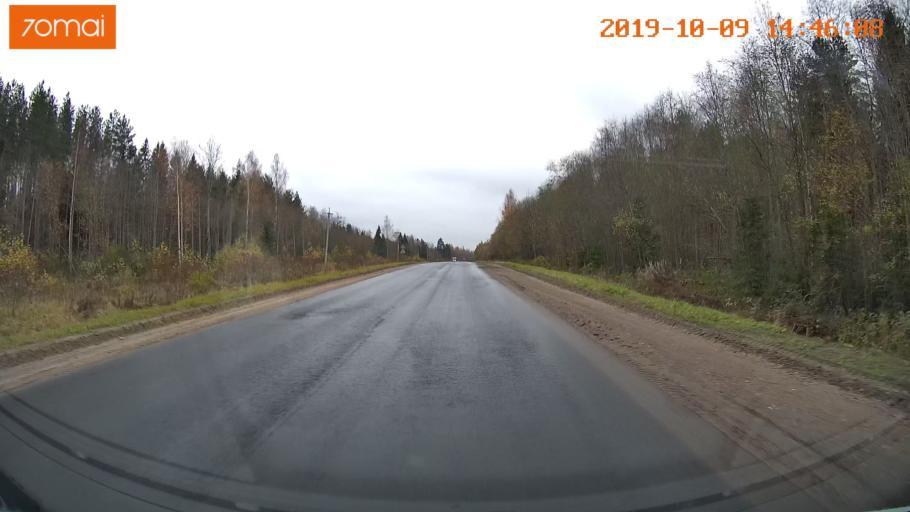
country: RU
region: Kostroma
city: Buy
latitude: 58.4352
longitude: 41.5772
